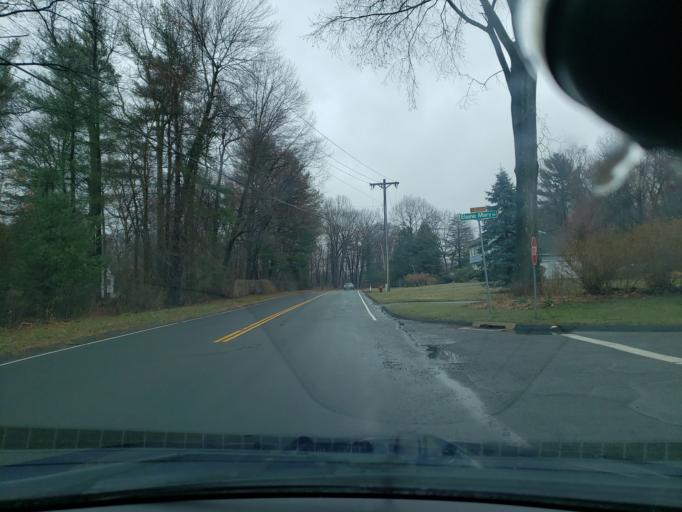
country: US
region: Connecticut
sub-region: Hartford County
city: Windsor
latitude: 41.8853
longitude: -72.6833
